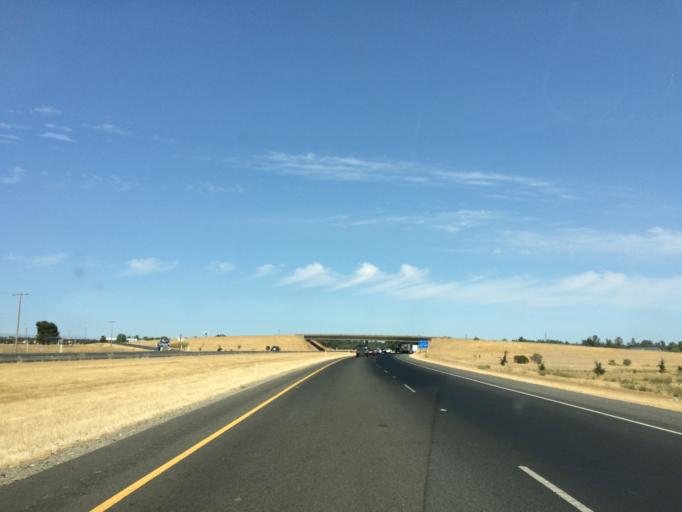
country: US
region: California
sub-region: Yolo County
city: Dunnigan
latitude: 38.8793
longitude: -121.9722
